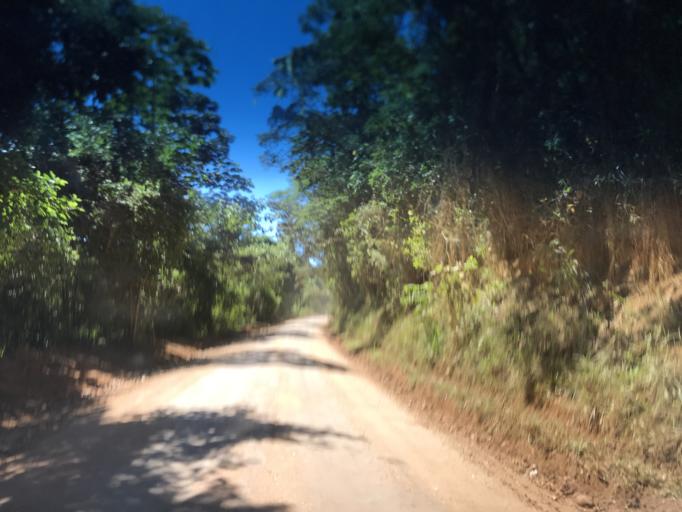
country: BR
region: Bahia
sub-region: Mutuipe
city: Mutuipe
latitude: -13.3740
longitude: -39.3770
